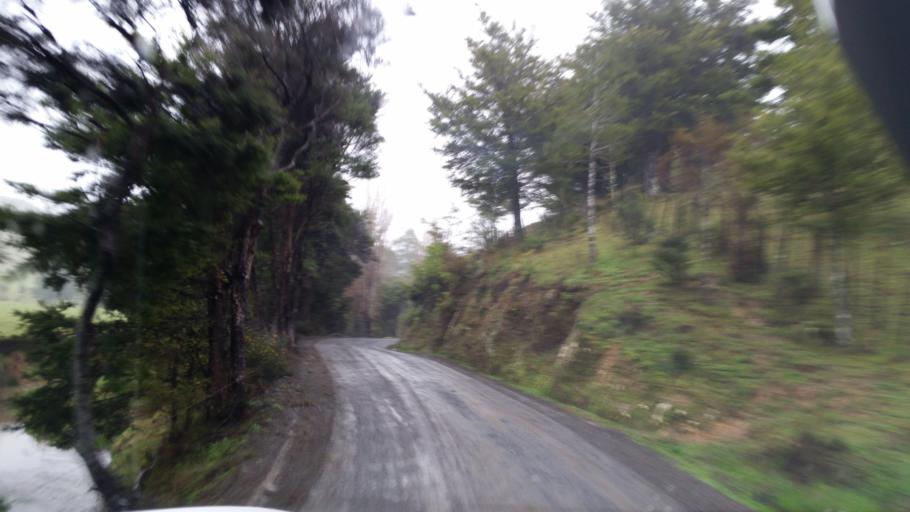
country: NZ
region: Northland
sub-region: Whangarei
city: Ngunguru
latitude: -35.4991
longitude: 174.4297
